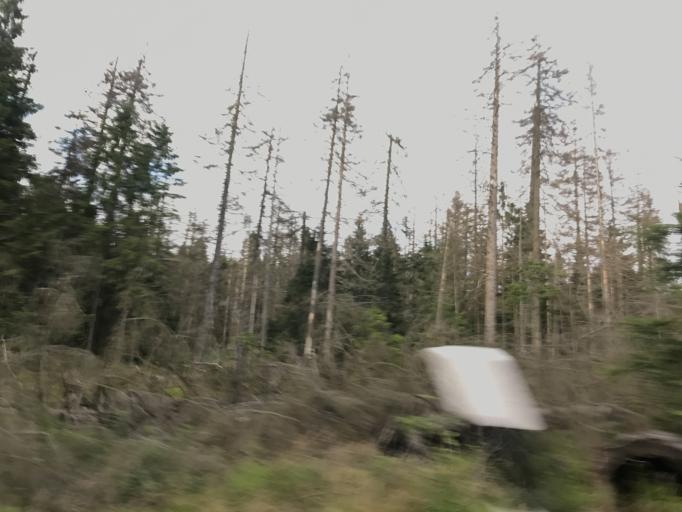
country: DE
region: Lower Saxony
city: Sankt Andreasberg
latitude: 51.7616
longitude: 10.5435
